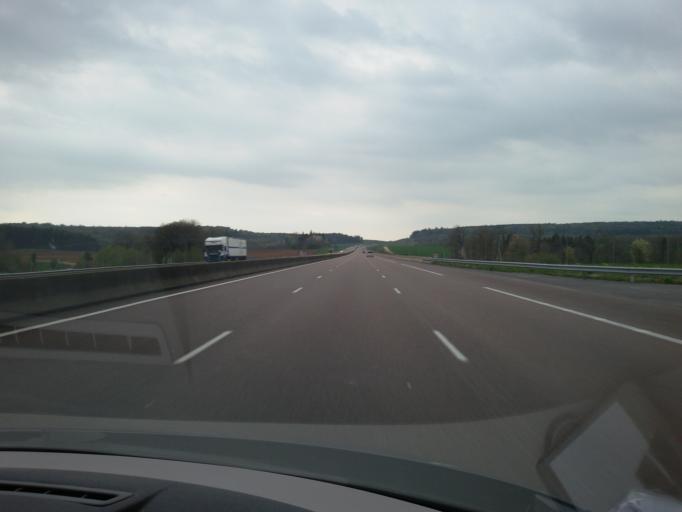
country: FR
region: Champagne-Ardenne
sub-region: Departement de la Haute-Marne
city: Langres
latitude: 47.8574
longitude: 5.2263
